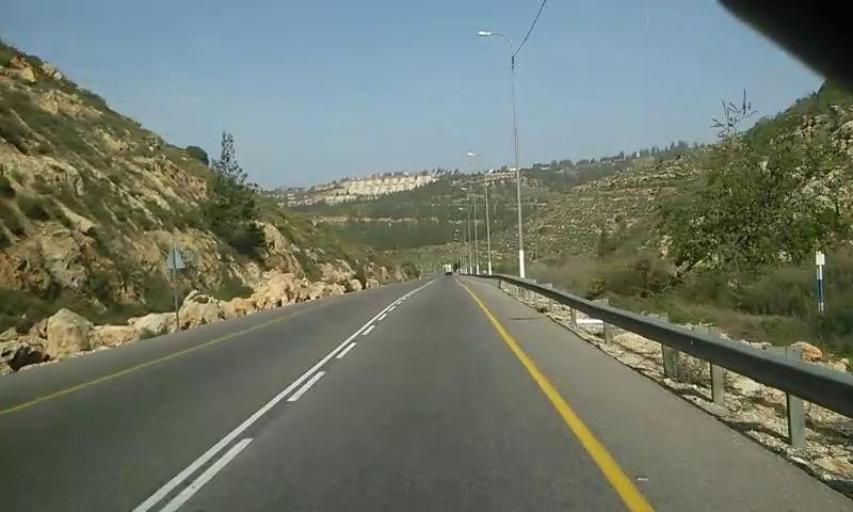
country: PS
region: West Bank
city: Qaryut
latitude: 32.0653
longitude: 35.2725
